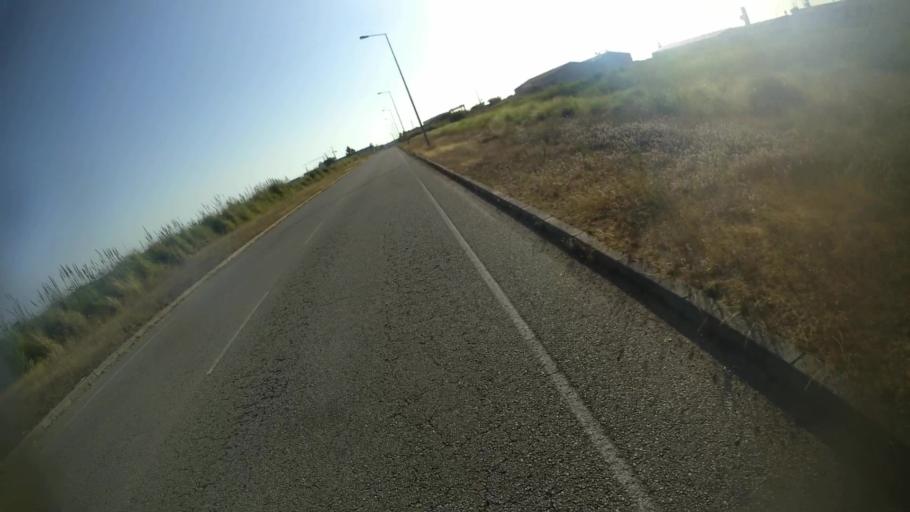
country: PT
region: Aveiro
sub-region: Aveiro
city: Aveiro
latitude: 40.6364
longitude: -8.6782
